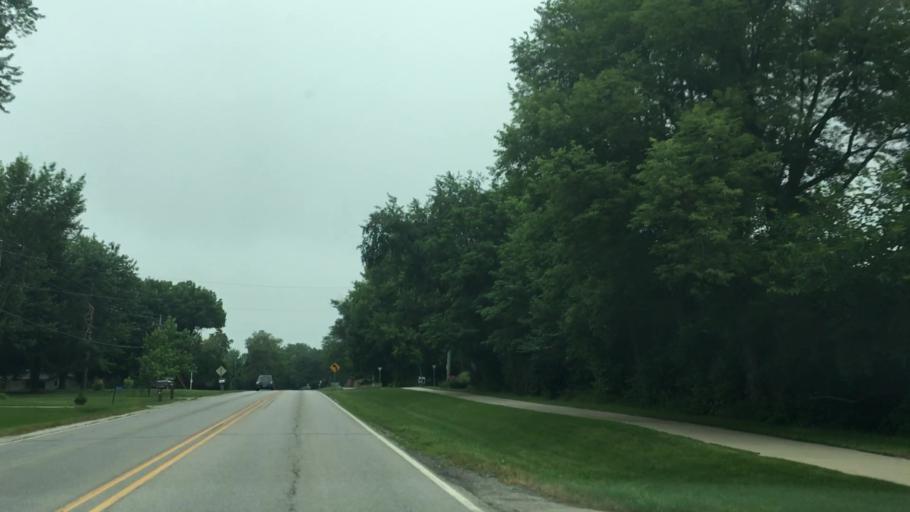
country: US
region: Iowa
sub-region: Johnson County
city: Coralville
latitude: 41.7171
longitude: -91.5524
